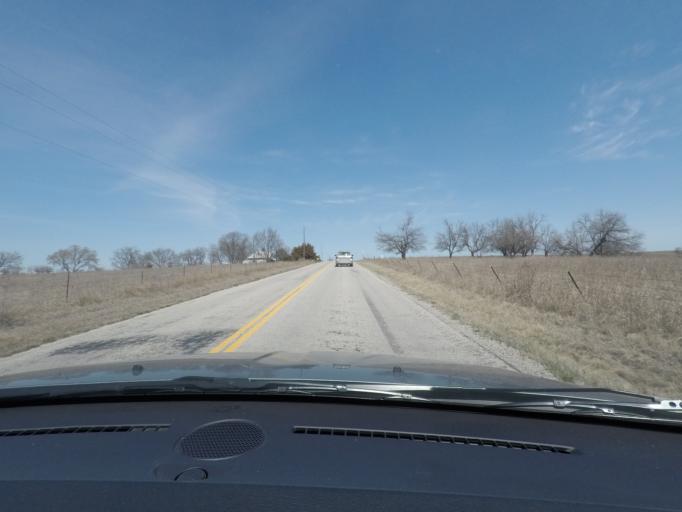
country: US
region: Kansas
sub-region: Lyon County
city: Emporia
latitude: 38.6212
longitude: -96.1696
